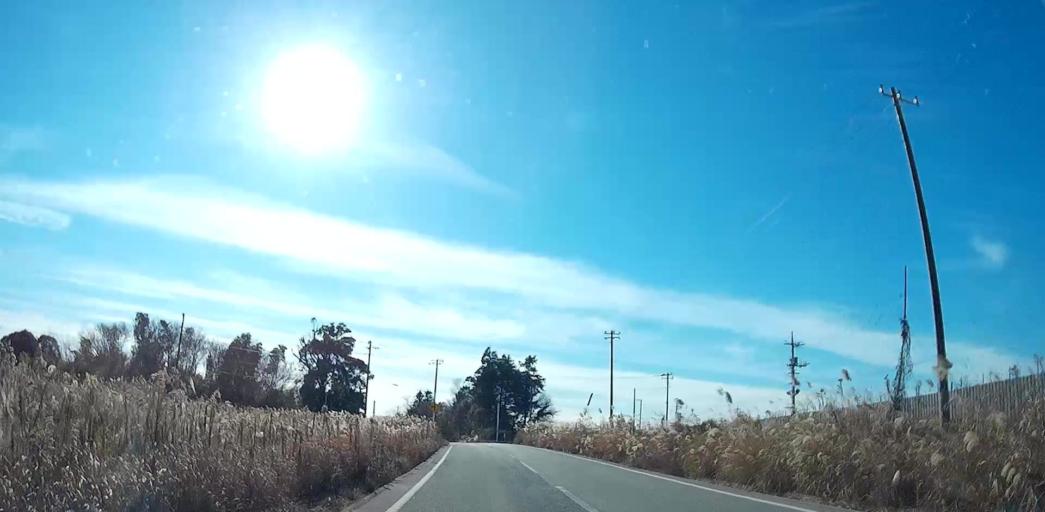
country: JP
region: Chiba
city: Narita
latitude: 35.7770
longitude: 140.4043
